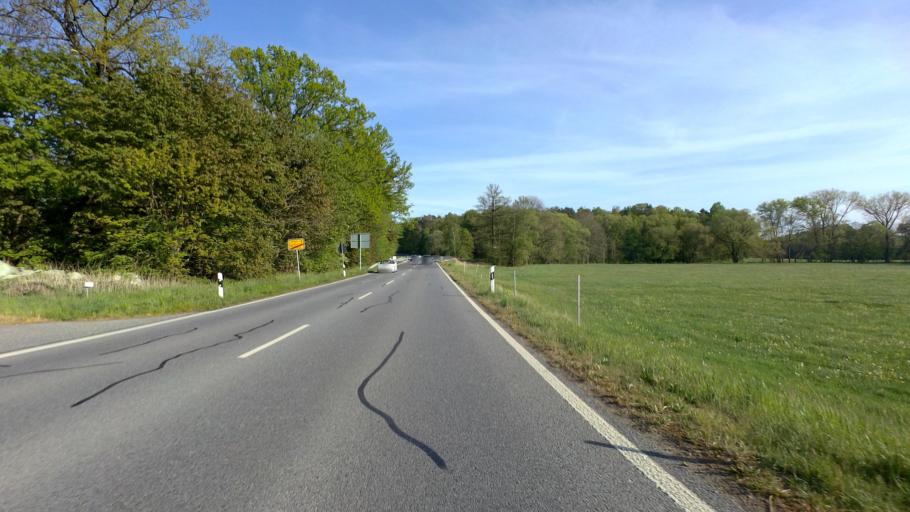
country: DE
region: Saxony
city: Stolpen
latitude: 51.0576
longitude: 14.0633
